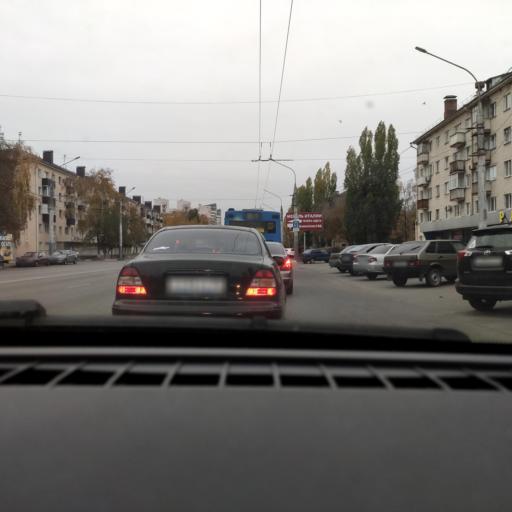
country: RU
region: Voronezj
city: Voronezh
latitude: 51.6679
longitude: 39.2502
